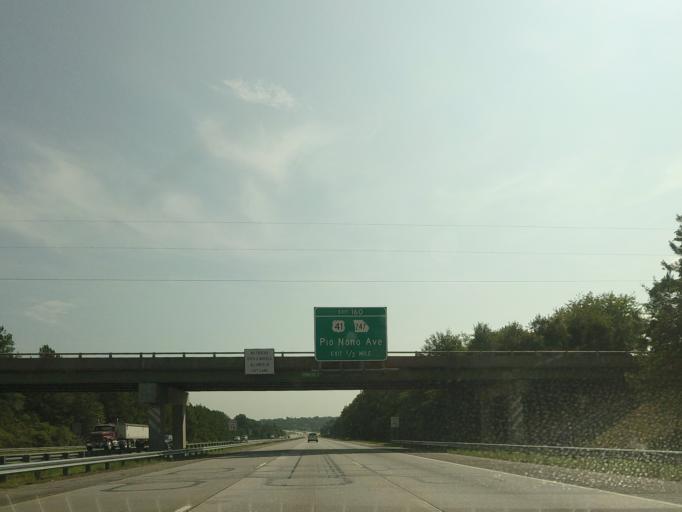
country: US
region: Georgia
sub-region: Bibb County
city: Macon
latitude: 32.7816
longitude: -83.6778
